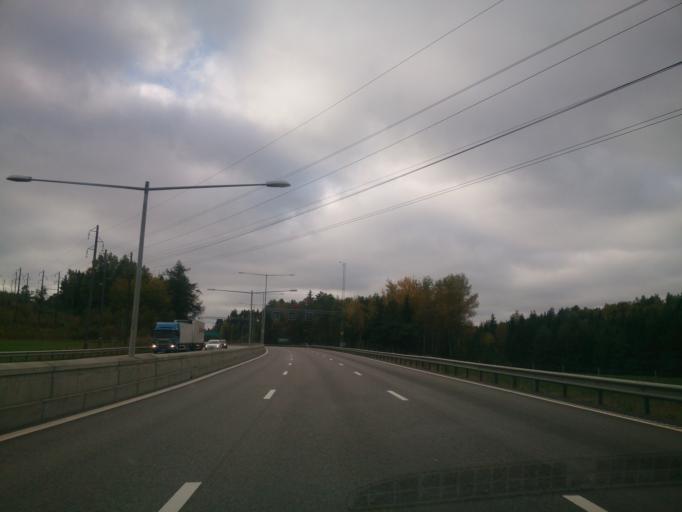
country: SE
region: Stockholm
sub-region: Botkyrka Kommun
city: Eriksberg
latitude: 59.2256
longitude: 17.7866
